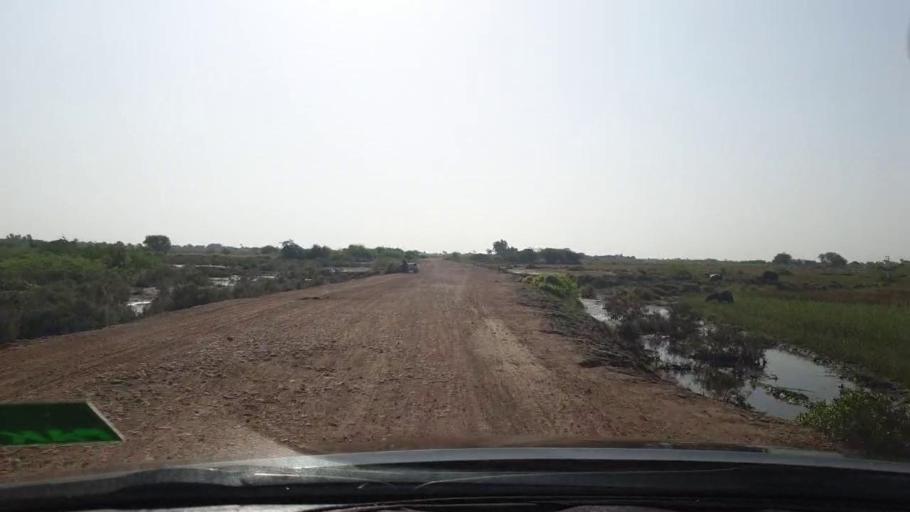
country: PK
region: Sindh
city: Tando Bago
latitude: 24.7183
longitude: 68.9668
